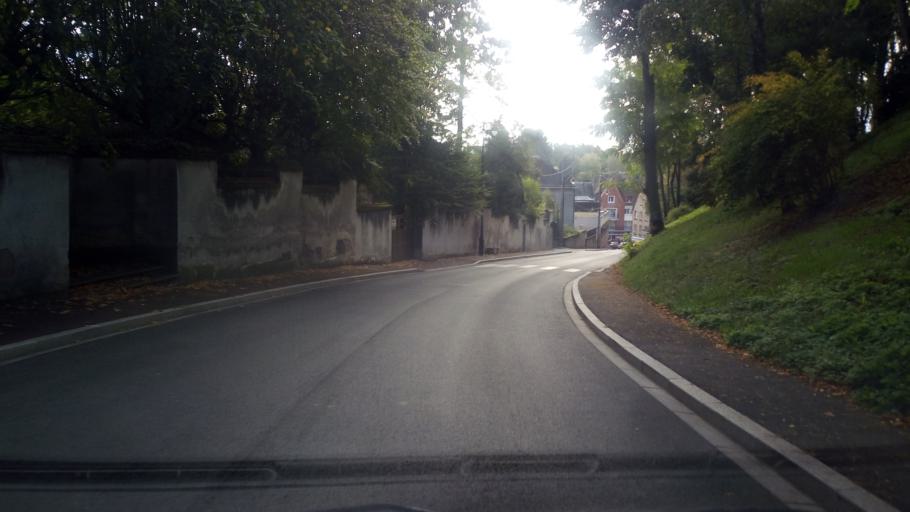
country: FR
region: Centre
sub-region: Departement du Loiret
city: Gien
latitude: 47.6858
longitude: 2.6313
